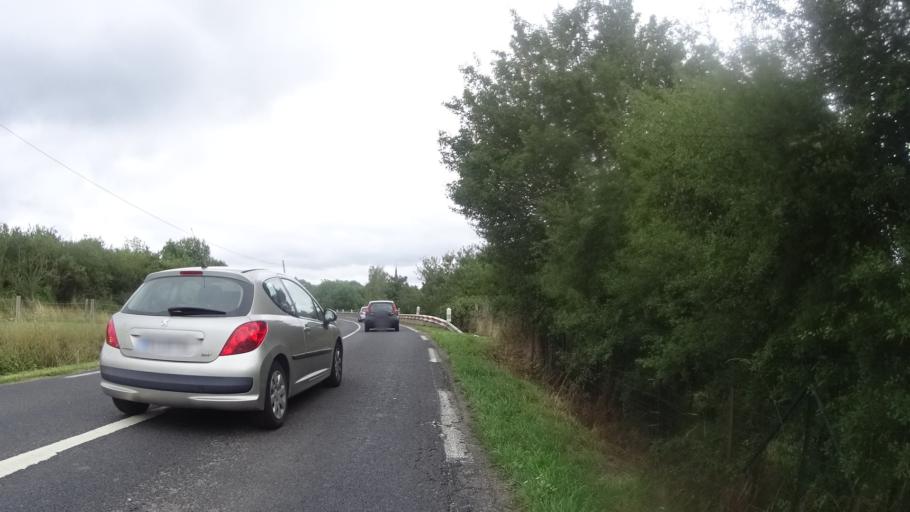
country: FR
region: Lorraine
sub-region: Departement de Meurthe-et-Moselle
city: Art-sur-Meurthe
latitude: 48.6514
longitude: 6.2705
